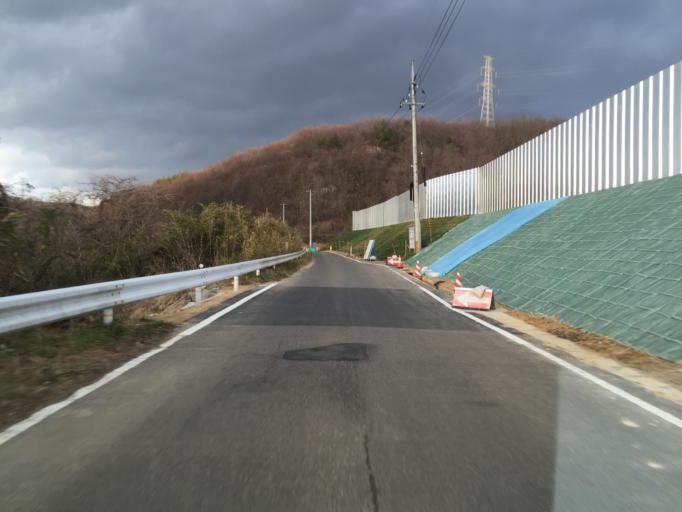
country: JP
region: Fukushima
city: Motomiya
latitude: 37.5271
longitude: 140.4151
